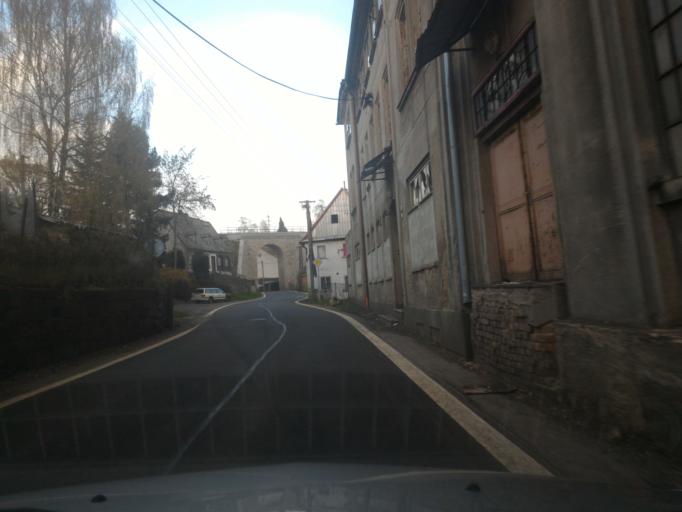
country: CZ
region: Ustecky
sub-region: Okres Decin
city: Krasna Lipa
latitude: 50.9141
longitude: 14.5177
